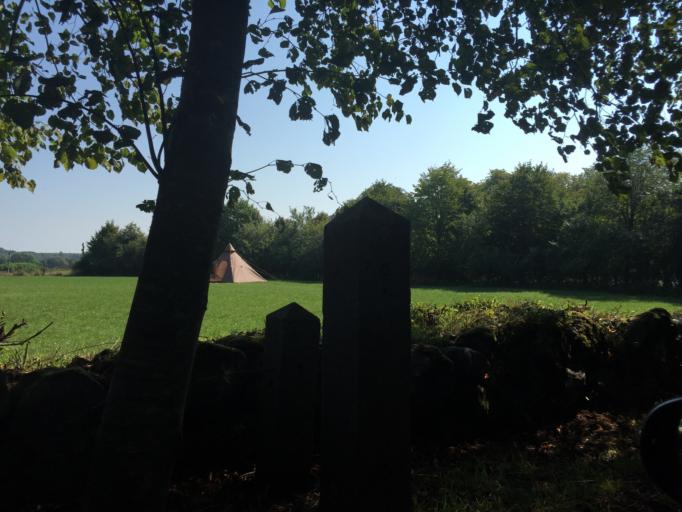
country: DK
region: South Denmark
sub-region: Langeland Kommune
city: Rudkobing
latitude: 54.8461
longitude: 10.7527
